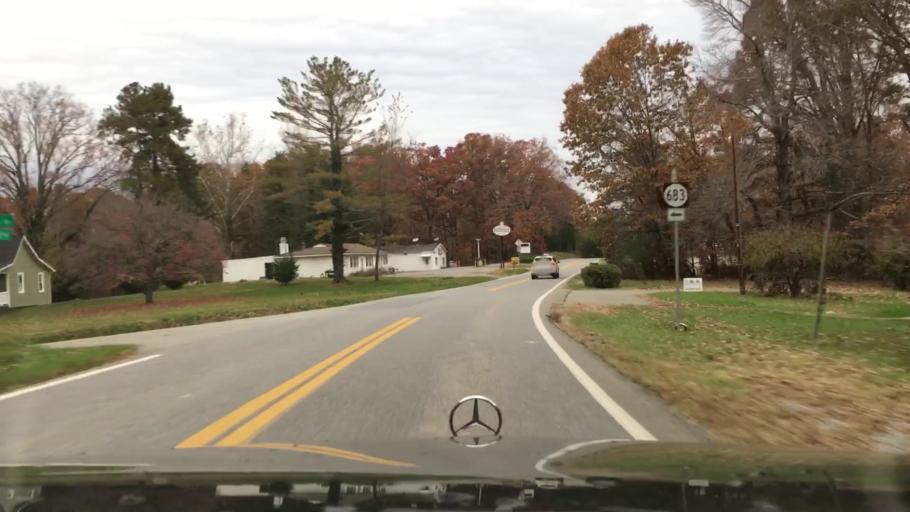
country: US
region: Virginia
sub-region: Campbell County
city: Timberlake
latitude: 37.2371
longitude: -79.2811
